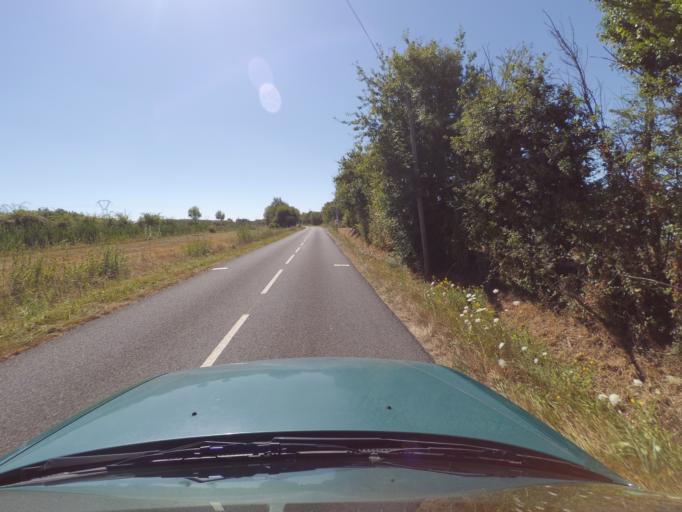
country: FR
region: Pays de la Loire
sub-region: Departement de la Loire-Atlantique
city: Le Bignon
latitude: 47.1177
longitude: -1.5043
